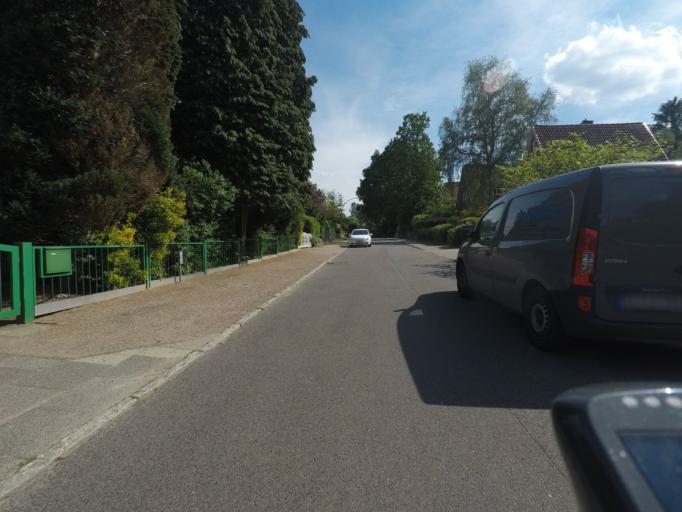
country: DE
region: Schleswig-Holstein
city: Barsbuettel
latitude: 53.6077
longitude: 10.1677
